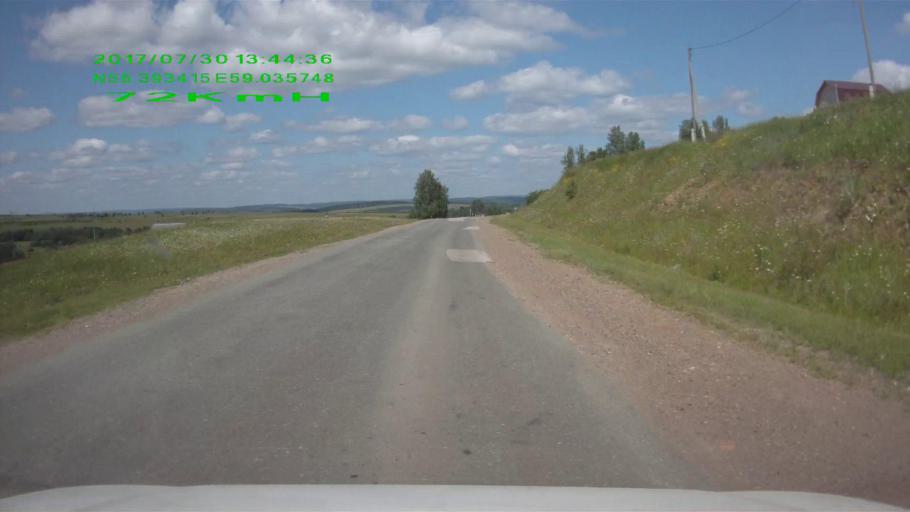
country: RU
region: Sverdlovsk
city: Mikhaylovsk
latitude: 56.3937
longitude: 59.0357
